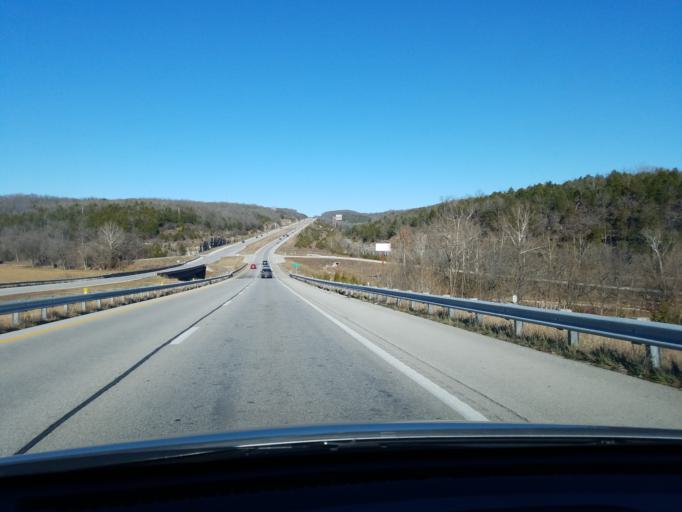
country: US
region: Missouri
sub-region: Taney County
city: Merriam Woods
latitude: 36.7675
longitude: -93.2236
